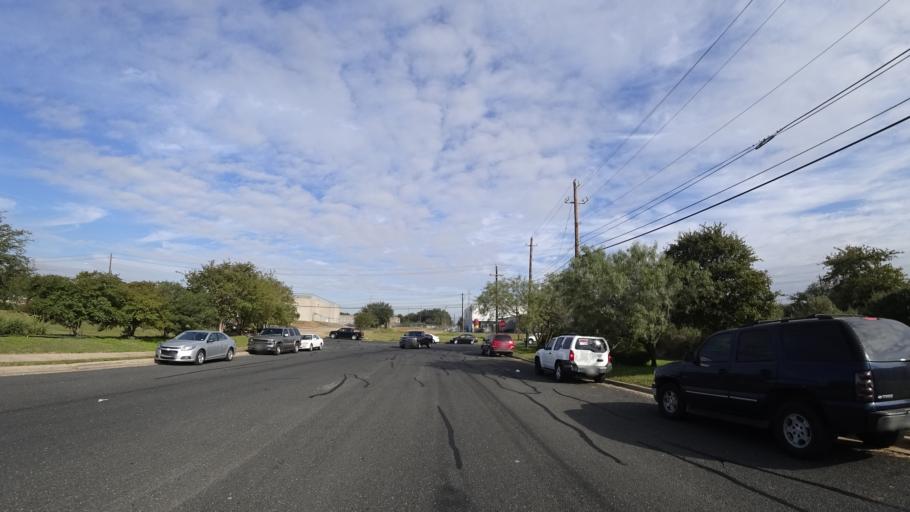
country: US
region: Texas
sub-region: Travis County
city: Austin
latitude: 30.2092
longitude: -97.7283
